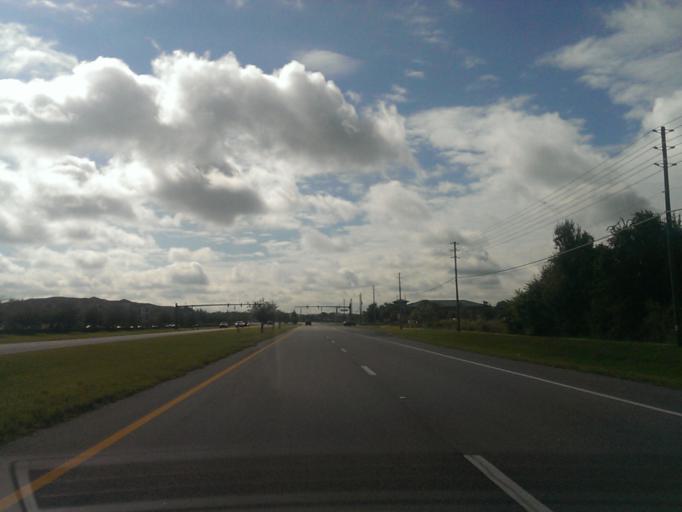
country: US
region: Florida
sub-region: Orange County
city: Bay Hill
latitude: 28.4514
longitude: -81.5620
